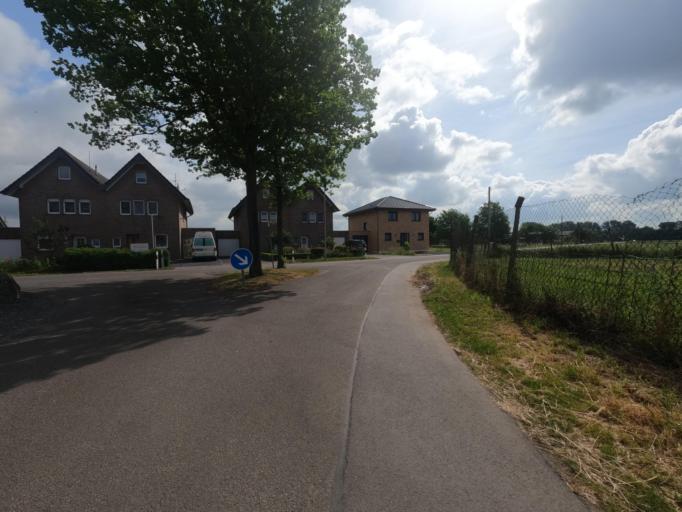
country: DE
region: North Rhine-Westphalia
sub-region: Regierungsbezirk Koln
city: Wassenberg
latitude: 51.0720
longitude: 6.1426
